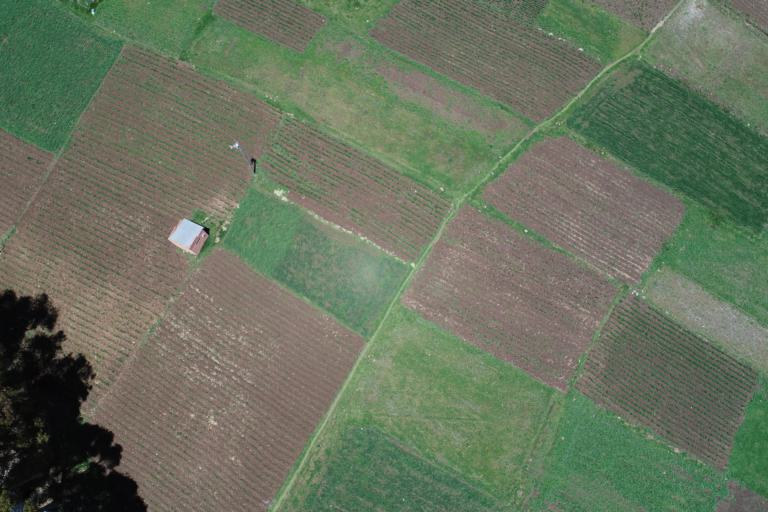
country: BO
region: La Paz
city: Achacachi
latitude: -16.0214
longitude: -68.7891
